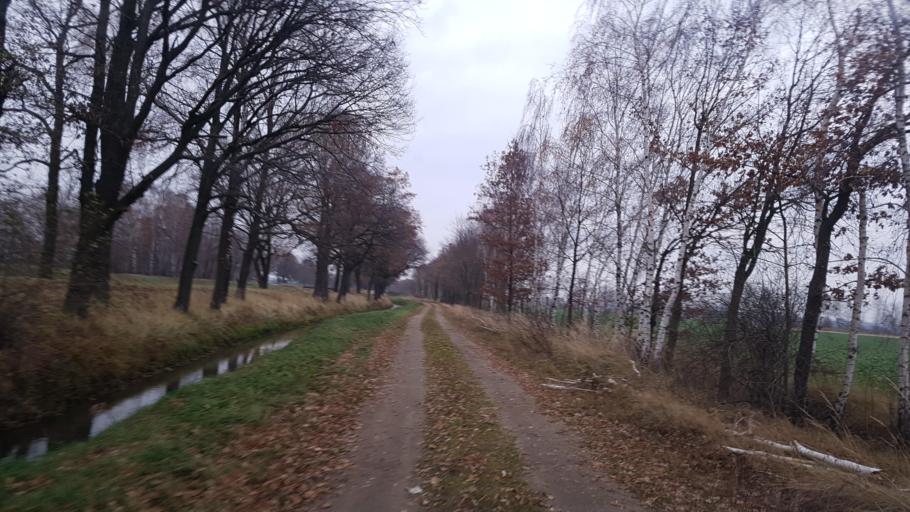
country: DE
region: Brandenburg
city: Hirschfeld
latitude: 51.4128
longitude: 13.6158
